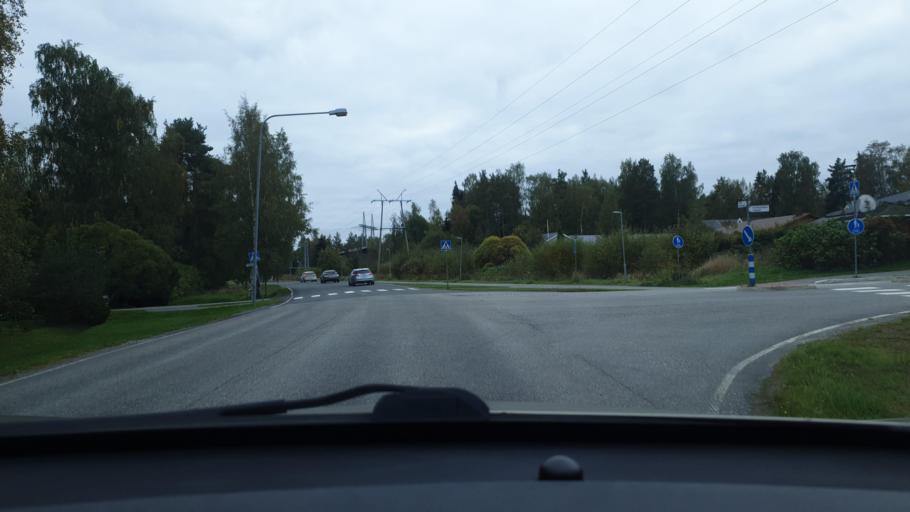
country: FI
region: Ostrobothnia
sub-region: Vaasa
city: Teeriniemi
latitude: 63.0948
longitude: 21.6975
